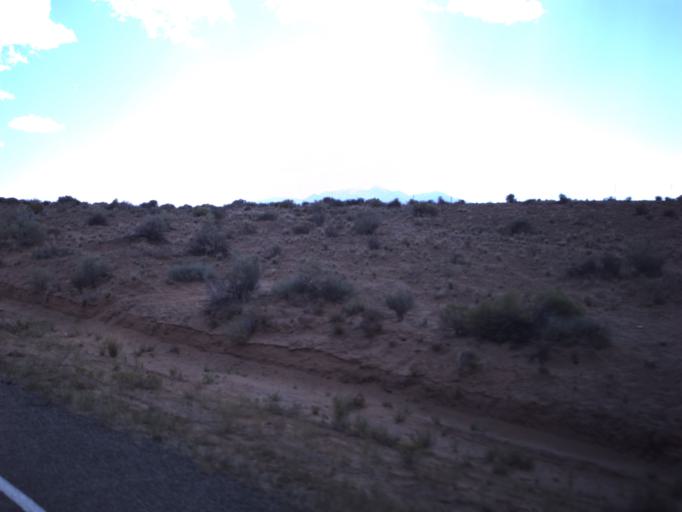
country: US
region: Utah
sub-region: Emery County
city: Ferron
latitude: 38.3542
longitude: -110.6964
